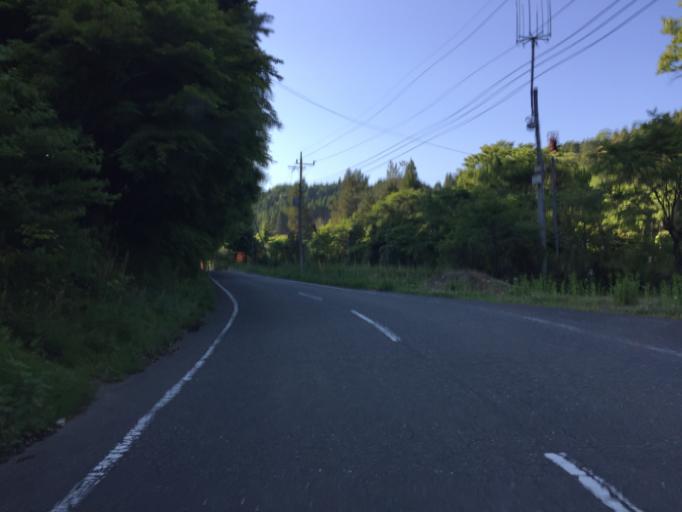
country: JP
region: Ibaraki
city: Kitaibaraki
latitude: 36.8681
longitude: 140.6369
